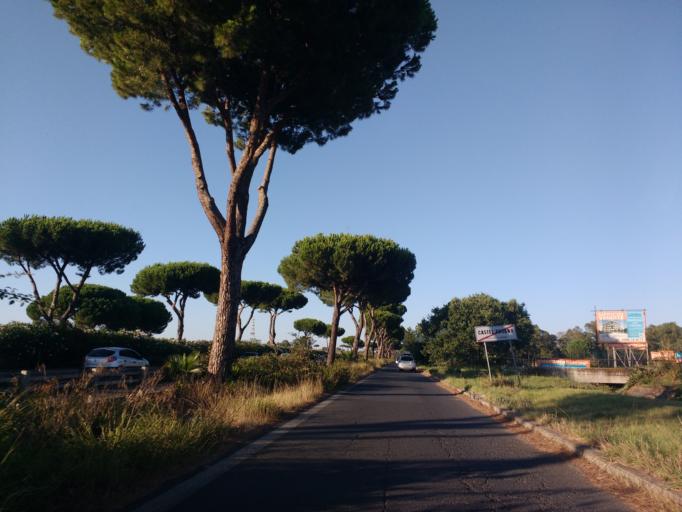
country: IT
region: Latium
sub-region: Citta metropolitana di Roma Capitale
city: Acilia-Castel Fusano-Ostia Antica
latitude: 41.7572
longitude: 12.3731
